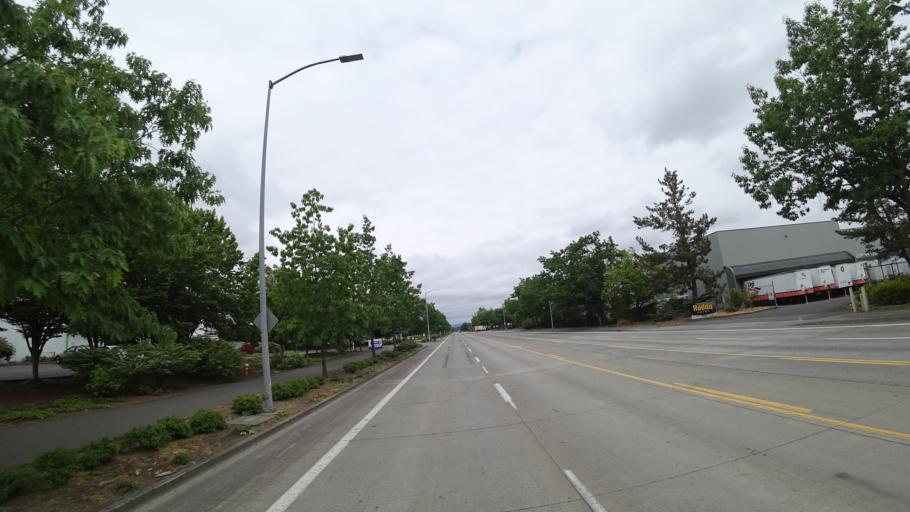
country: US
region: Washington
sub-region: Clark County
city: Vancouver
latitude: 45.6253
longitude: -122.7364
